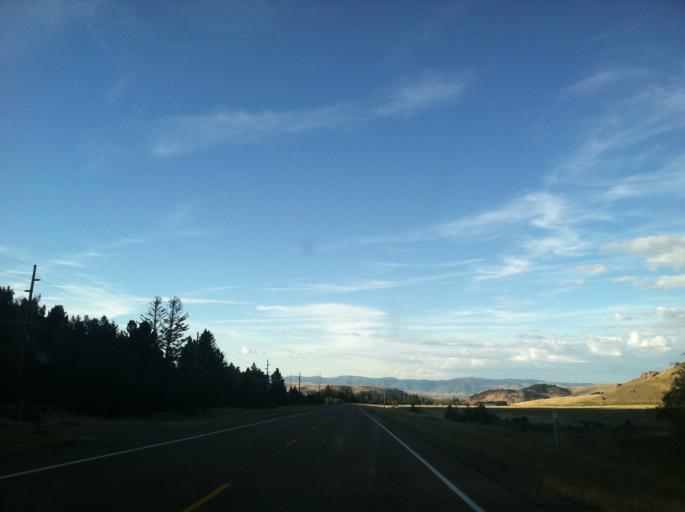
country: US
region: Montana
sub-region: Granite County
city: Philipsburg
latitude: 46.4771
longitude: -113.2346
